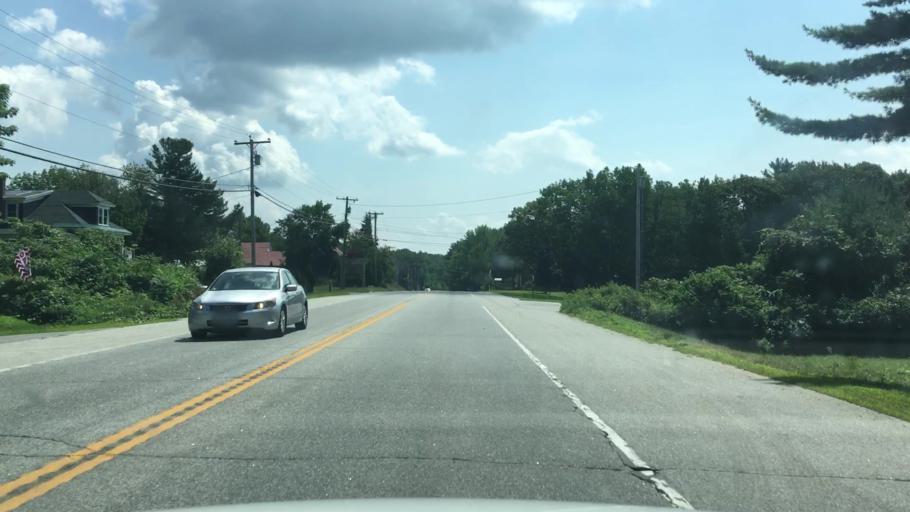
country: US
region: Maine
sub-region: Cumberland County
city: Raymond
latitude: 43.9263
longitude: -70.5323
